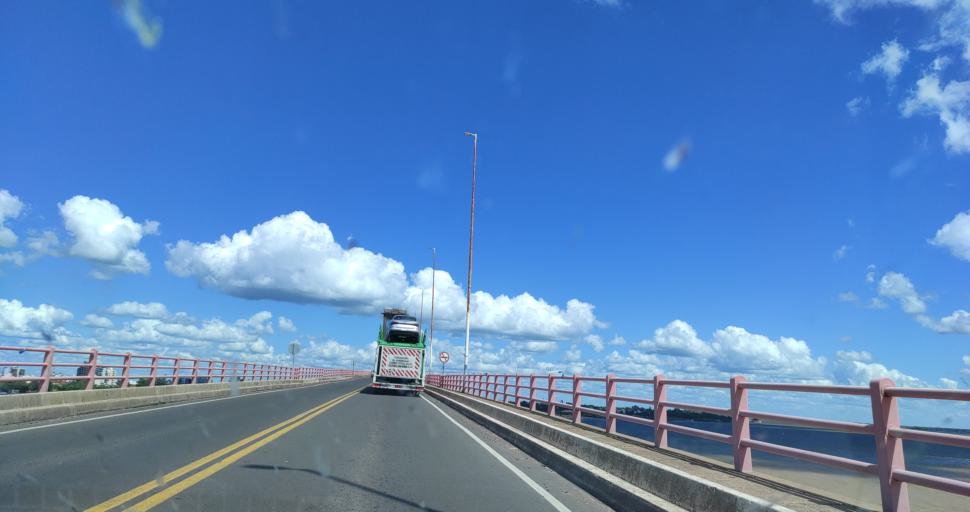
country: AR
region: Corrientes
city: Corrientes
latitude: -27.4666
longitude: -58.8652
